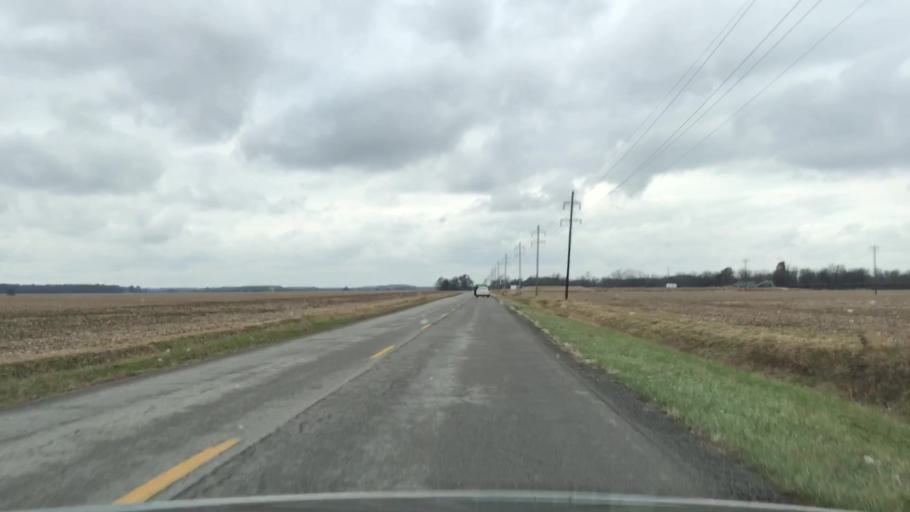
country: US
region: Kentucky
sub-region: McLean County
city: Calhoun
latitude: 37.5216
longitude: -87.2869
